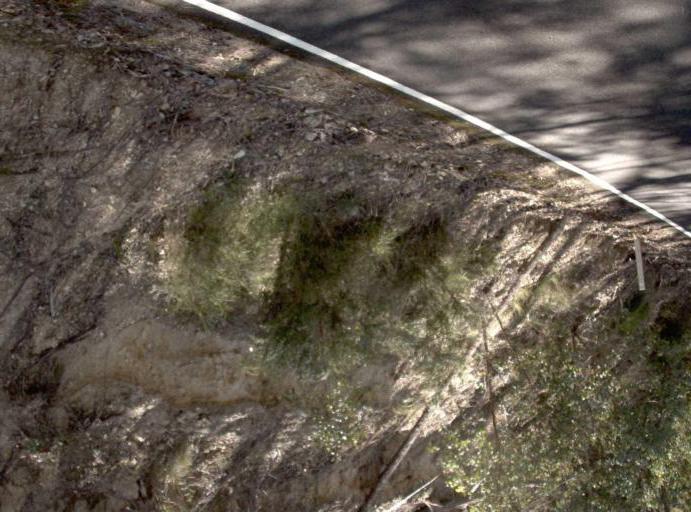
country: AU
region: Victoria
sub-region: East Gippsland
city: Lakes Entrance
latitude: -37.3843
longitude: 148.2186
